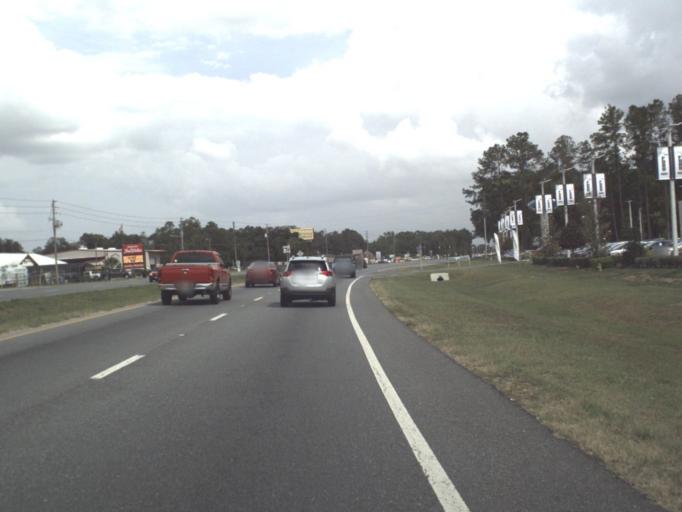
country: US
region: Florida
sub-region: Marion County
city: Belleview
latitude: 29.0535
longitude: -82.0403
